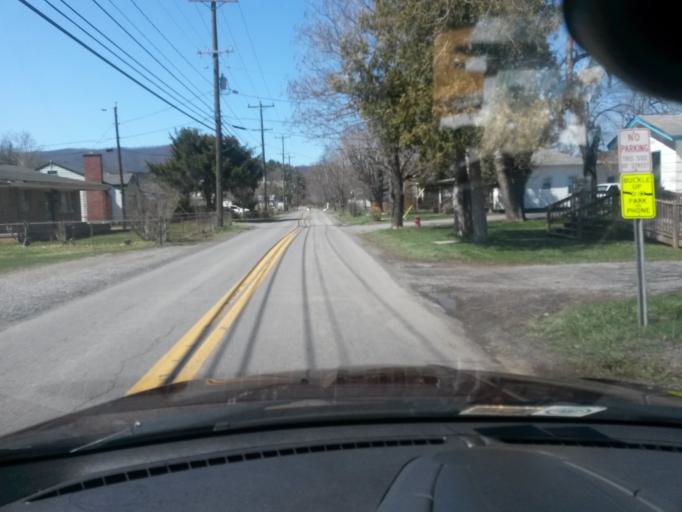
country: US
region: West Virginia
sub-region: Greenbrier County
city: White Sulphur Springs
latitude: 37.7892
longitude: -80.2895
